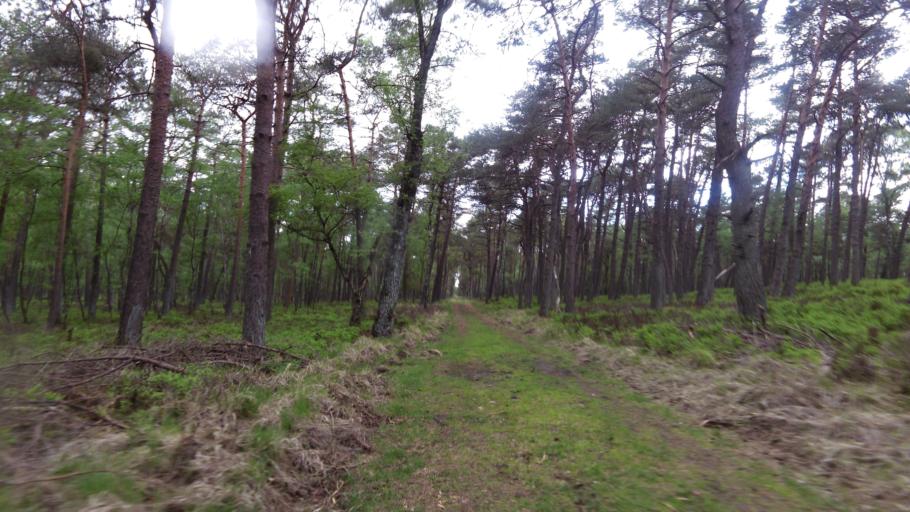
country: NL
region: Gelderland
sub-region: Gemeente Apeldoorn
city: Loenen
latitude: 52.0717
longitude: 6.0200
